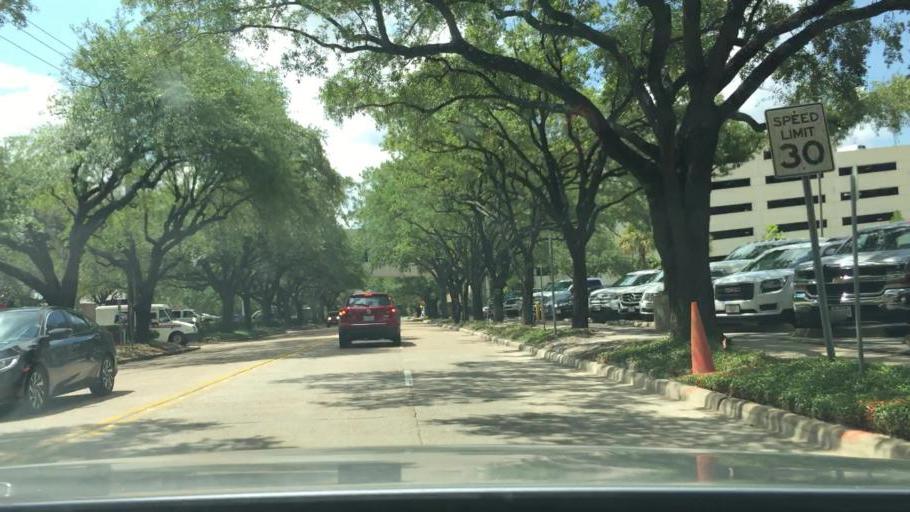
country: US
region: Texas
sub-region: Harris County
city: Bunker Hill Village
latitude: 29.7830
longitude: -95.5478
